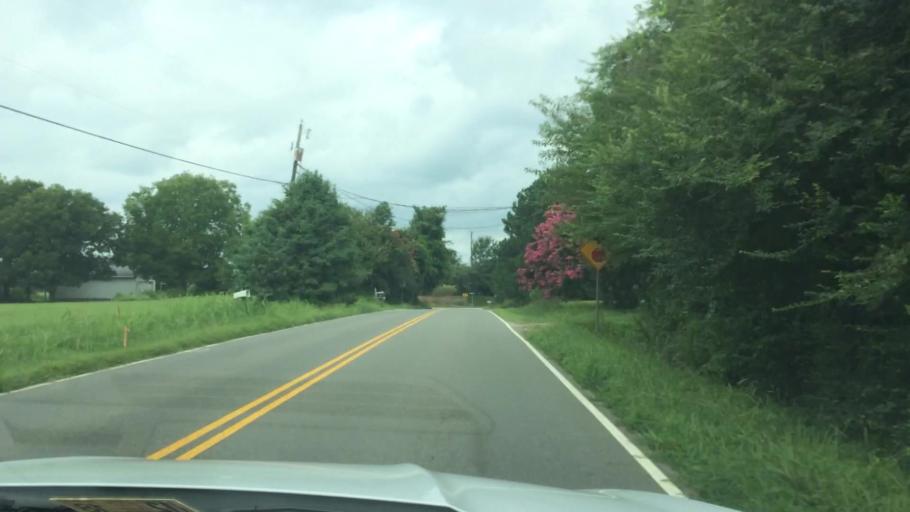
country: US
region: Virginia
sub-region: James City County
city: Williamsburg
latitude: 37.2809
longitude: -76.8031
